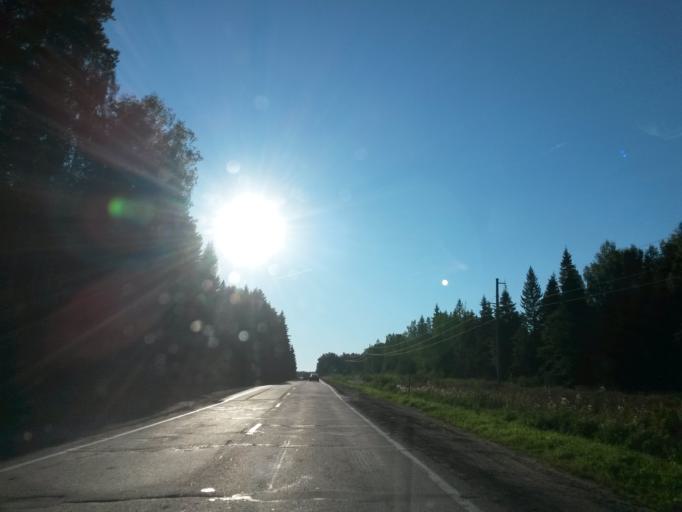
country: RU
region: Jaroslavl
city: Gavrilov-Yam
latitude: 57.2678
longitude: 39.9828
